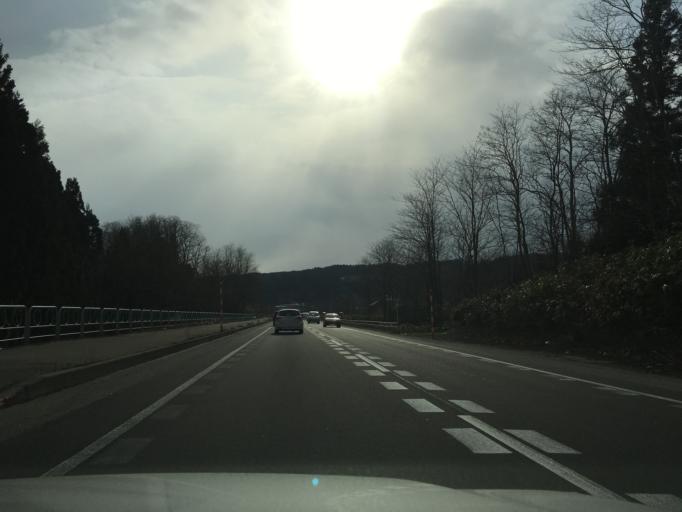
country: JP
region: Aomori
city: Namioka
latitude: 40.7695
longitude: 140.5950
